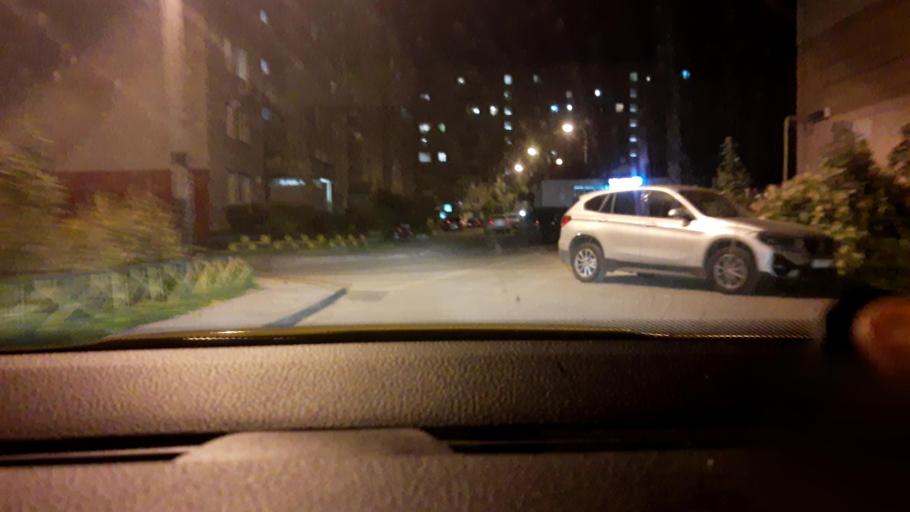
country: RU
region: Moskovskaya
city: Lobnya
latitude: 56.0102
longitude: 37.4774
